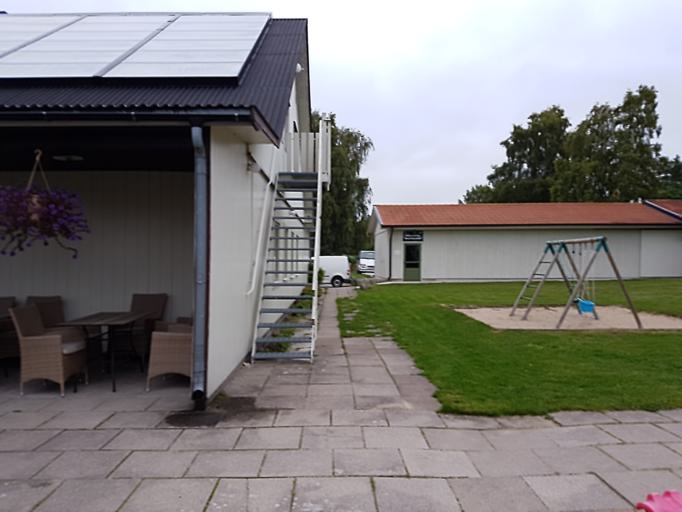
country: SE
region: Gotland
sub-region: Gotland
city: Klintehamn
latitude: 57.4857
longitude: 18.1401
